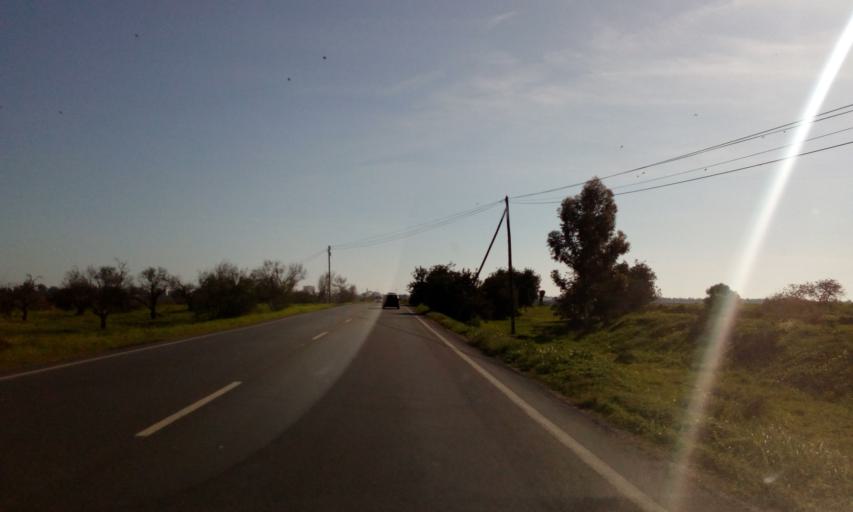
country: PT
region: Faro
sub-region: Castro Marim
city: Castro Marim
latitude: 37.2077
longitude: -7.4356
